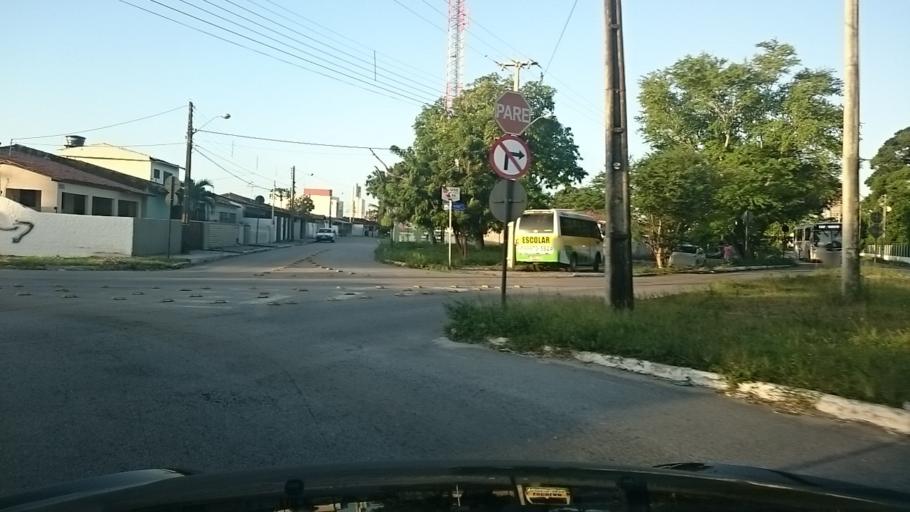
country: BR
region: Paraiba
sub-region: Joao Pessoa
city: Joao Pessoa
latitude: -7.1322
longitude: -34.8444
